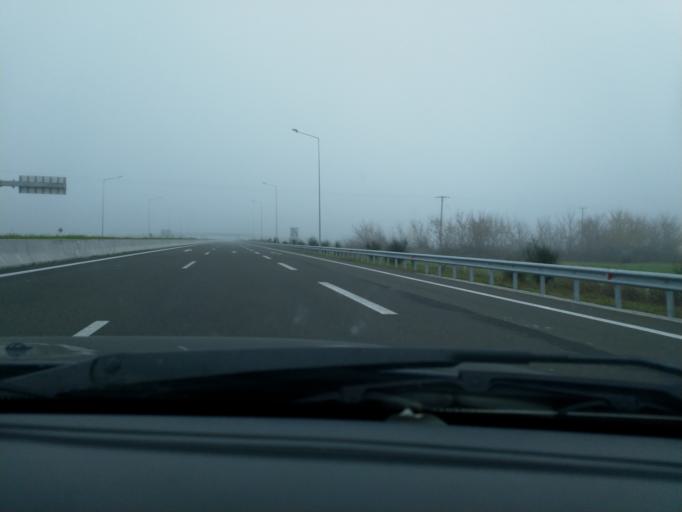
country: GR
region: Thessaly
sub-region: Nomos Kardhitsas
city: Sofades
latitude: 39.3114
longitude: 22.0643
